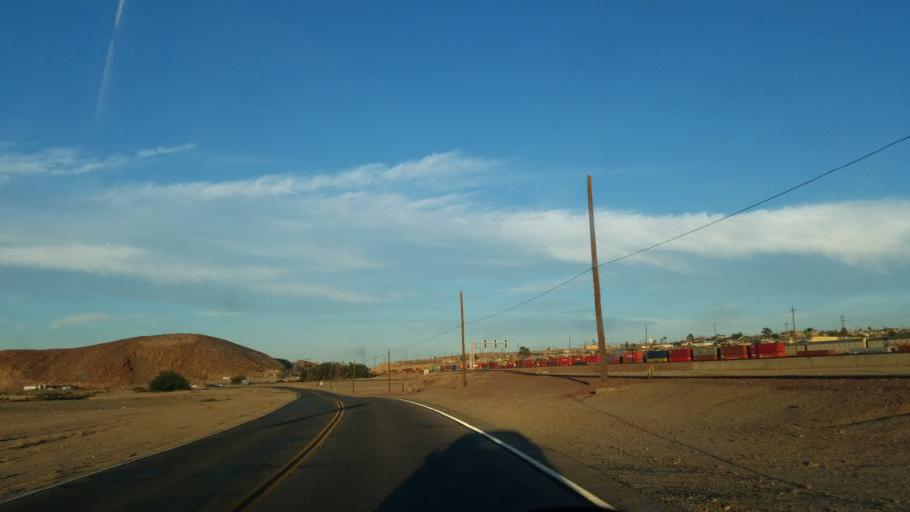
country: US
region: California
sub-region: San Bernardino County
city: Barstow
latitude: 34.9046
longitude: -117.0211
